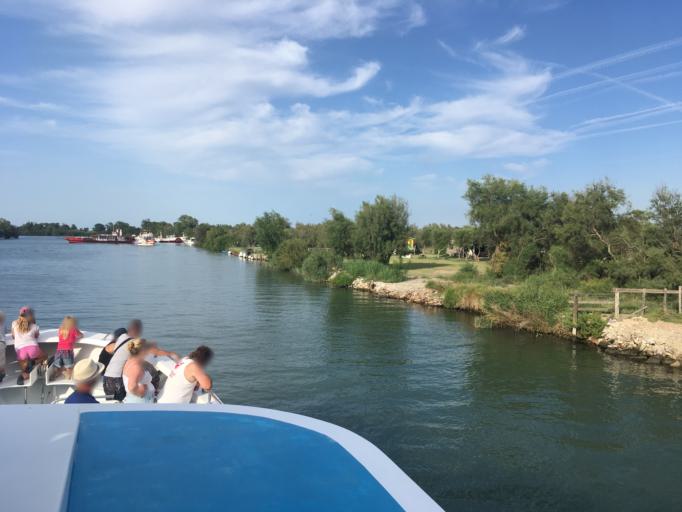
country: FR
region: Provence-Alpes-Cote d'Azur
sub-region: Departement des Bouches-du-Rhone
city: Saintes-Maries-de-la-Mer
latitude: 43.4848
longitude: 4.3816
